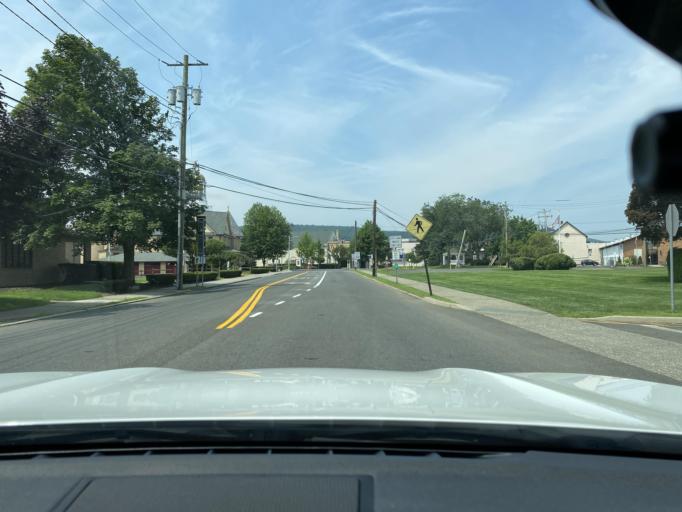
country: US
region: New York
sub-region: Rockland County
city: Suffern
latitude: 41.1151
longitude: -74.1479
